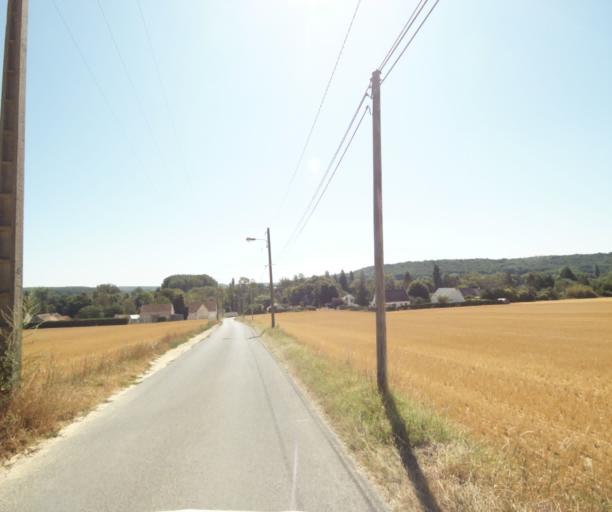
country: FR
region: Ile-de-France
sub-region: Departement de l'Essonne
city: Baulne
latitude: 48.4995
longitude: 2.3537
